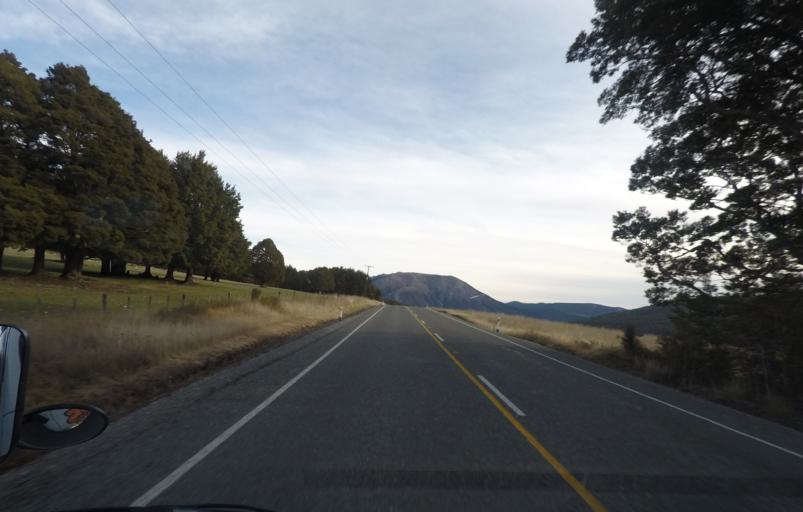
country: NZ
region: Tasman
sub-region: Tasman District
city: Wakefield
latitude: -41.7914
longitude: 172.8810
